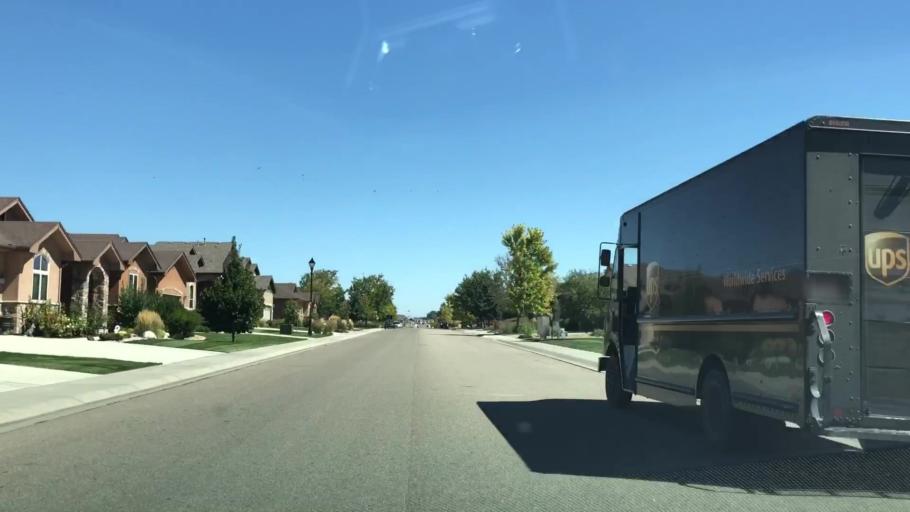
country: US
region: Colorado
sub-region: Weld County
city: Johnstown
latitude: 40.3993
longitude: -104.9793
